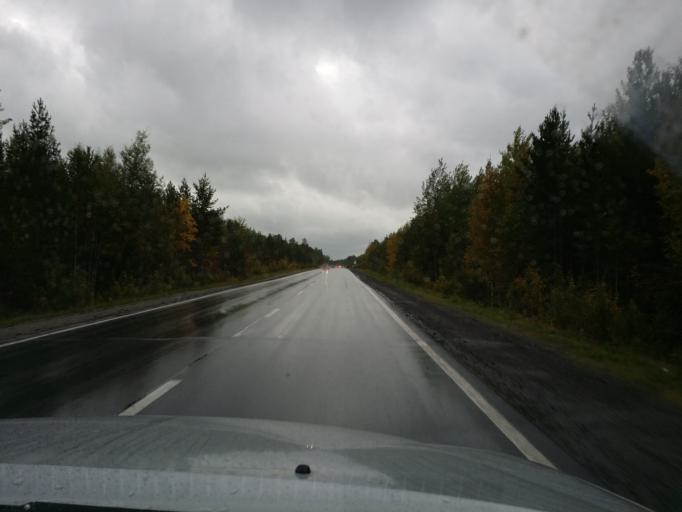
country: RU
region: Khanty-Mansiyskiy Avtonomnyy Okrug
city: Megion
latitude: 61.1101
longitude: 75.8457
